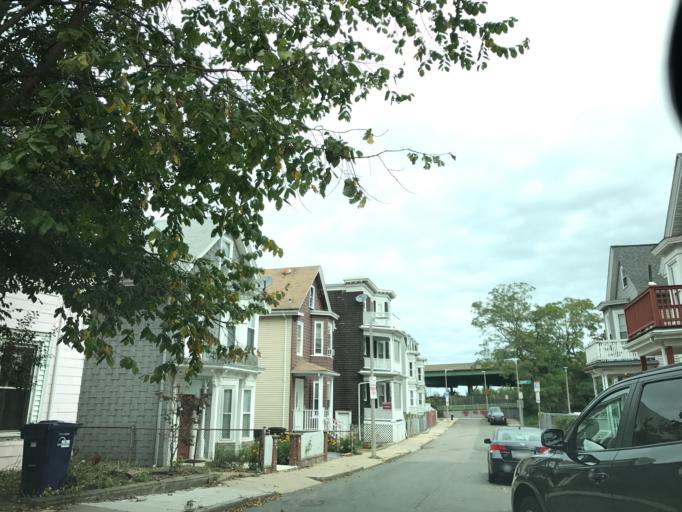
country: US
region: Massachusetts
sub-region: Suffolk County
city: South Boston
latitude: 42.3204
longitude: -71.0547
